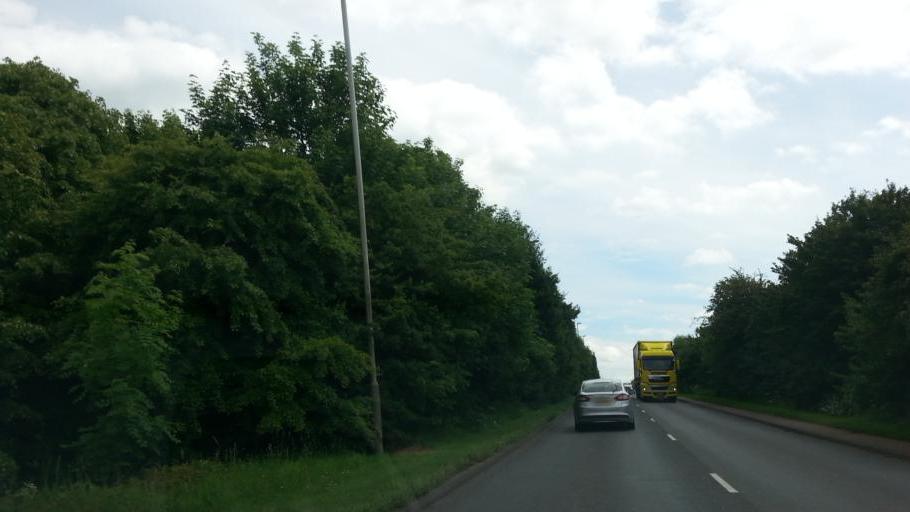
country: GB
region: England
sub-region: Leicestershire
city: Syston
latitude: 52.6647
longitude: -1.0976
